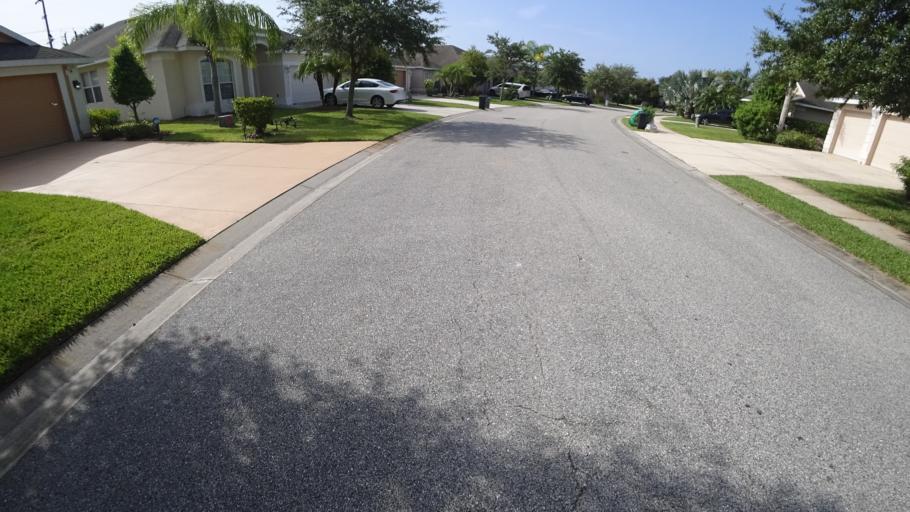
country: US
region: Florida
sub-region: Manatee County
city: Ellenton
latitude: 27.5551
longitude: -82.5000
